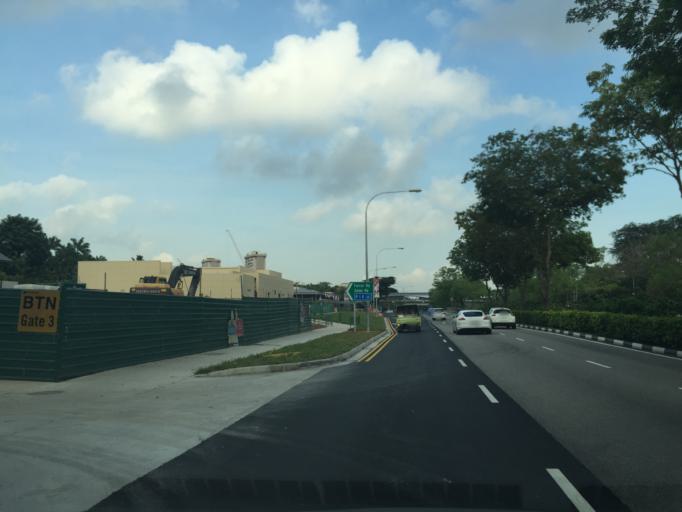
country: SG
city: Singapore
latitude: 1.3226
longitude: 103.8175
